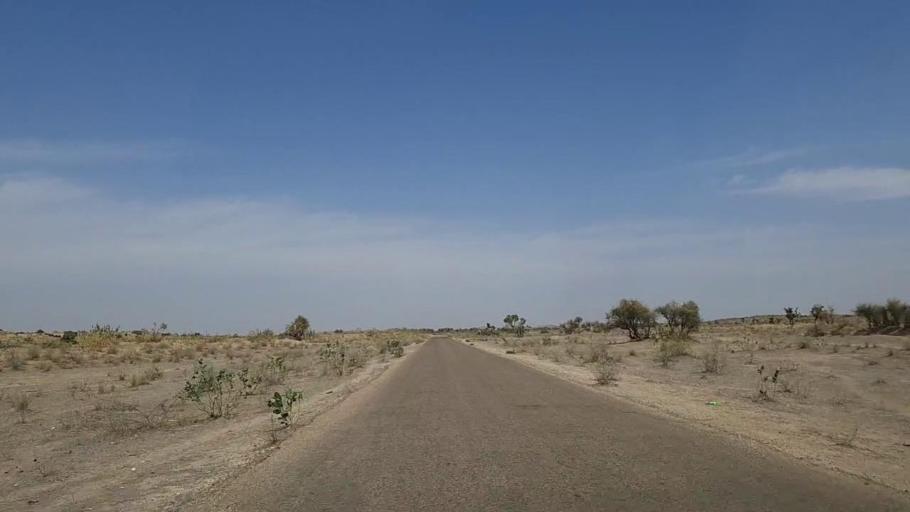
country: PK
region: Sindh
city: Nabisar
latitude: 25.0718
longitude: 69.9729
